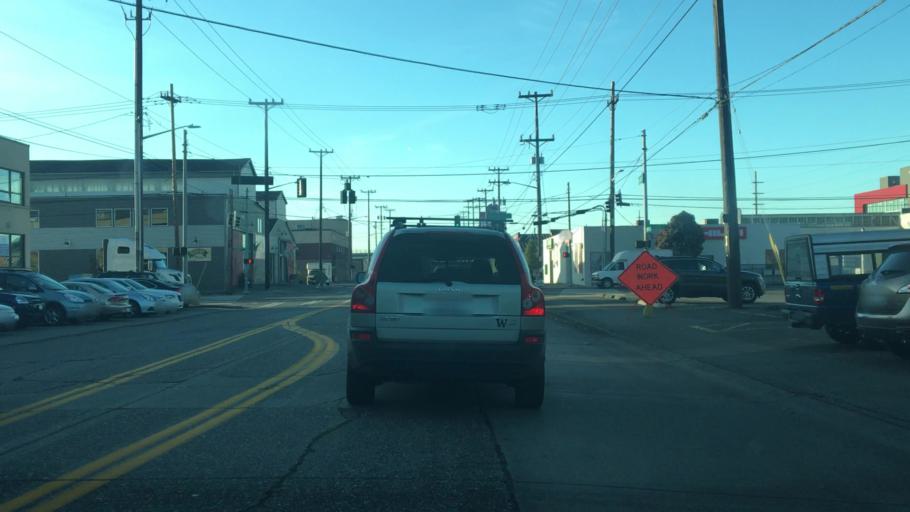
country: US
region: Washington
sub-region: King County
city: Seattle
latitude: 47.5803
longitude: -122.3260
